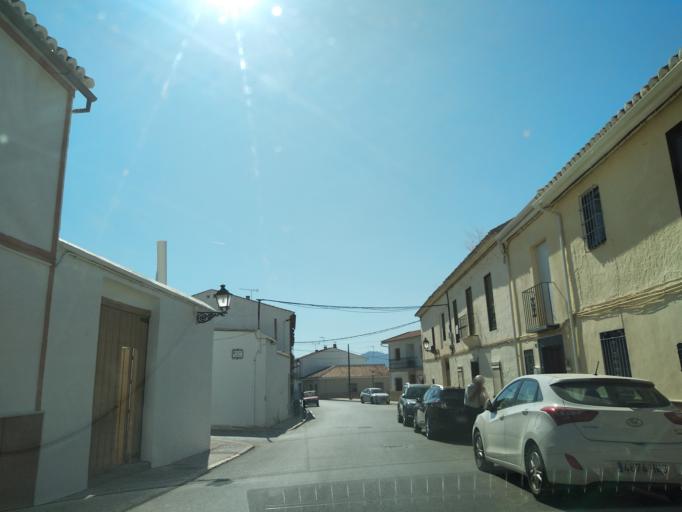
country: ES
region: Andalusia
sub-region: Provincia de Malaga
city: Mollina
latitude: 37.1242
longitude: -4.6567
